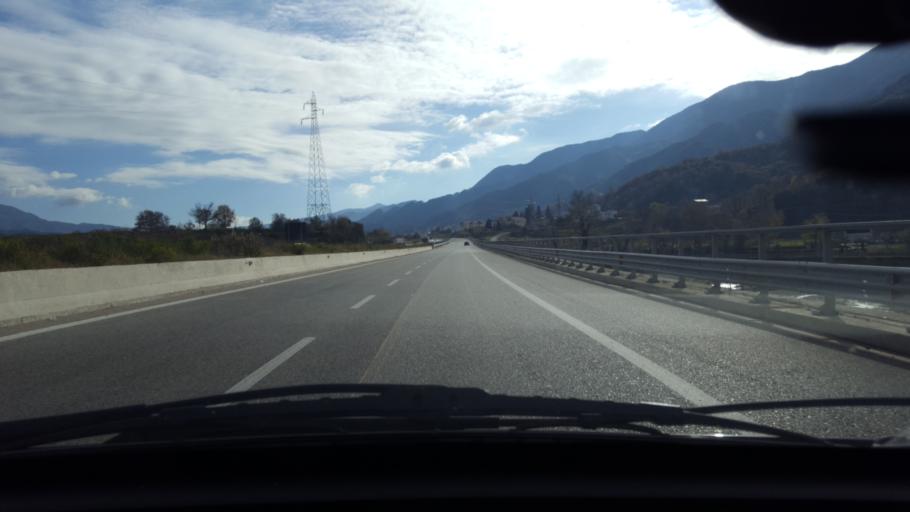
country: AL
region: Tirane
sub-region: Rrethi i Tiranes
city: Berzhite
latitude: 41.2581
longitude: 19.8909
